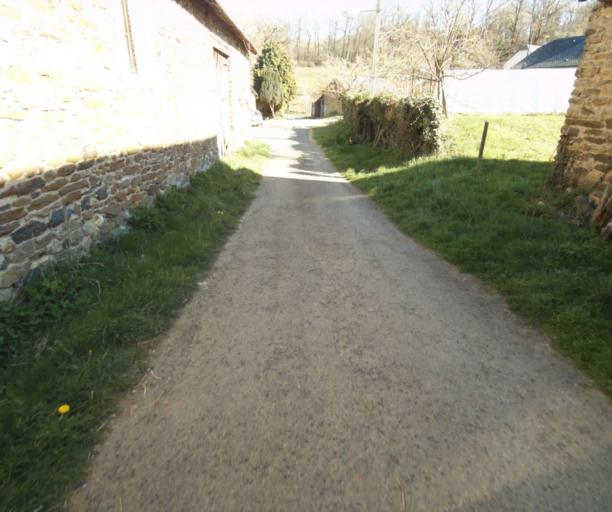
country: FR
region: Limousin
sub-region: Departement de la Correze
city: Chamboulive
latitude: 45.4113
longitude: 1.6558
